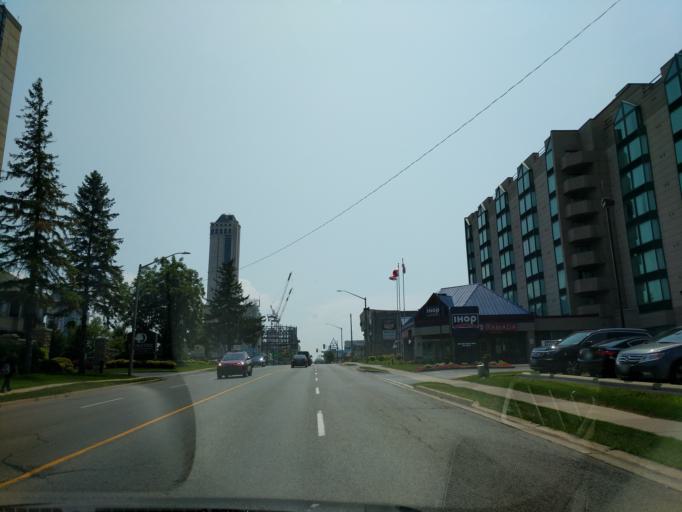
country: CA
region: Ontario
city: Niagara Falls
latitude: 43.0878
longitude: -79.0848
